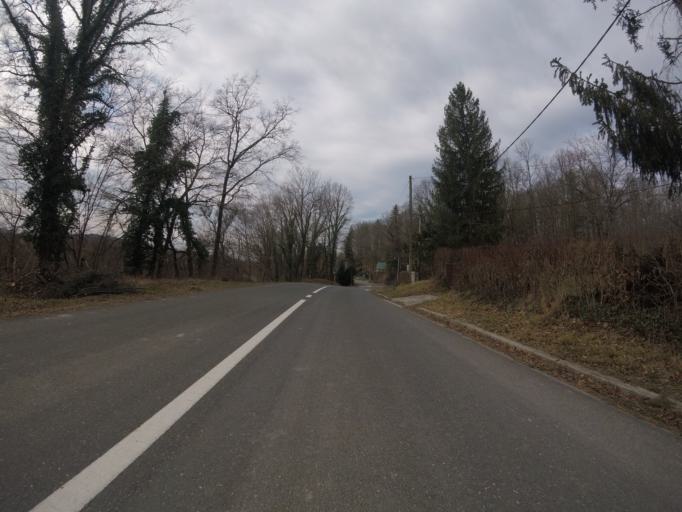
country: HR
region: Sisacko-Moslavacka
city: Glina
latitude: 45.4894
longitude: 16.0146
